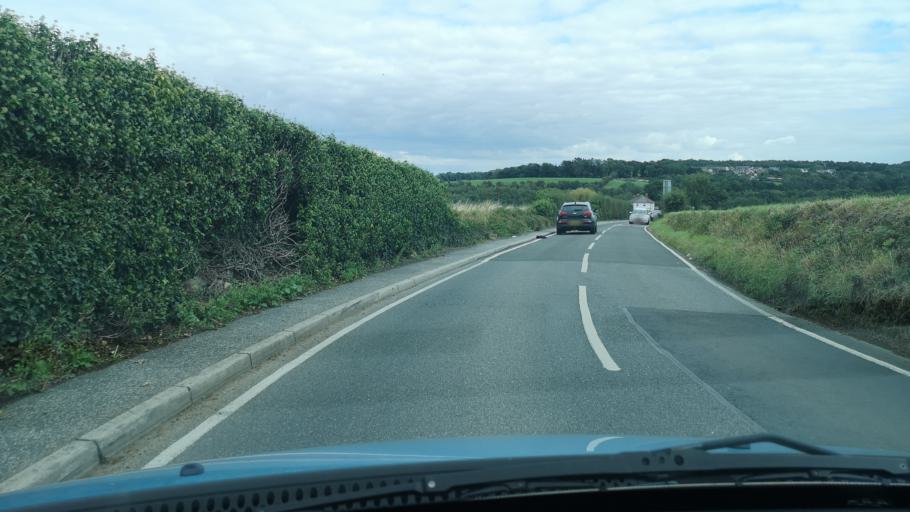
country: GB
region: England
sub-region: City and Borough of Wakefield
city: Horbury
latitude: 53.6445
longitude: -1.5561
